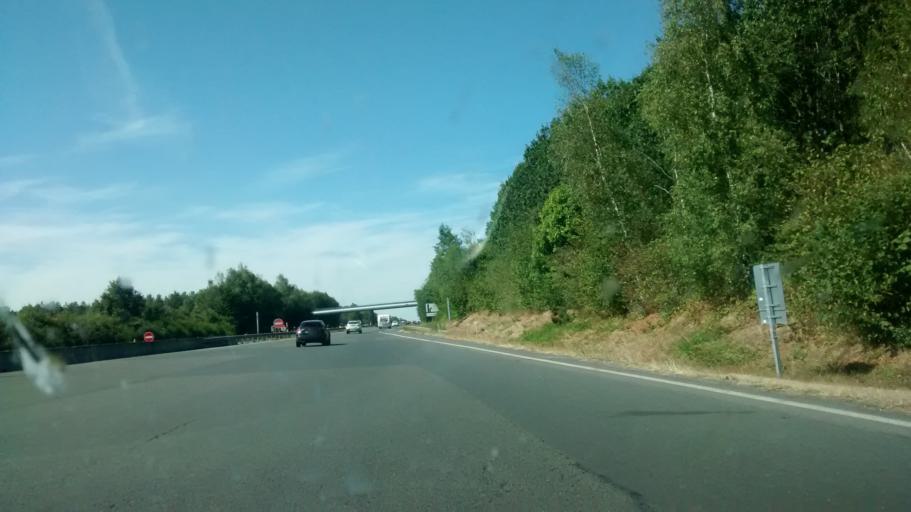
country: FR
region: Pays de la Loire
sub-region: Departement de la Loire-Atlantique
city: Le Bignon
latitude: 47.1169
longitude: -1.4938
